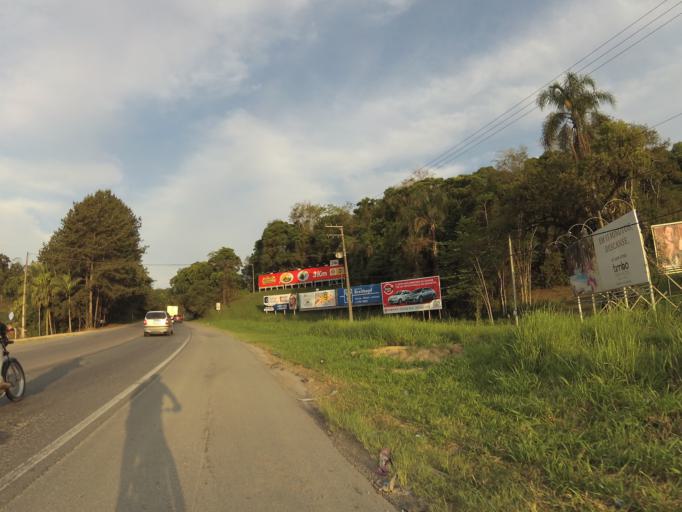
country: BR
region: Santa Catarina
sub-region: Indaial
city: Indaial
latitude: -26.8830
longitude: -49.1563
